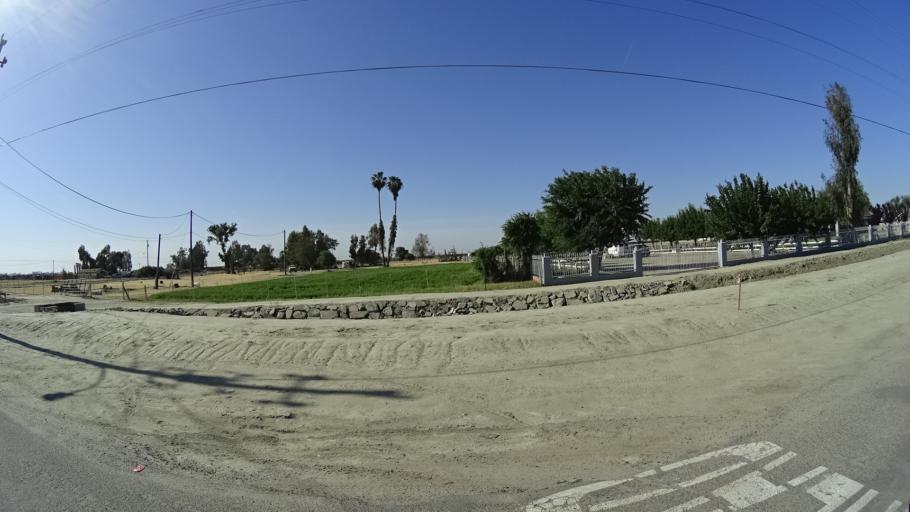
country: US
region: California
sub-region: Kings County
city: Corcoran
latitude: 36.0944
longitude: -119.5911
